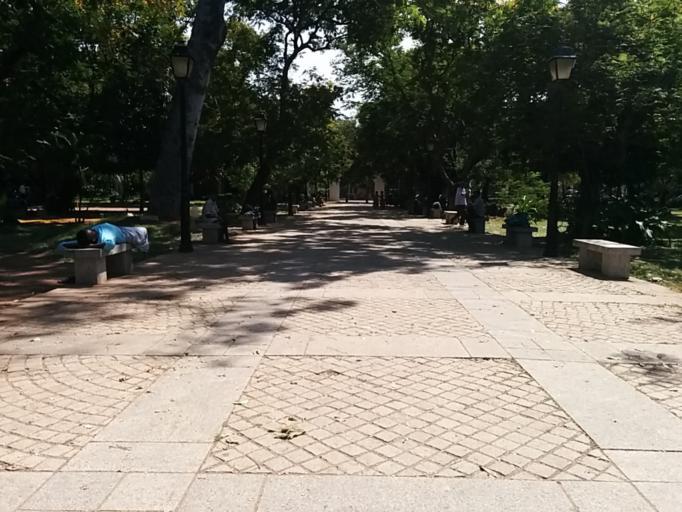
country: IN
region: Pondicherry
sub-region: Puducherry
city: Puducherry
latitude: 11.9327
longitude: 79.8341
